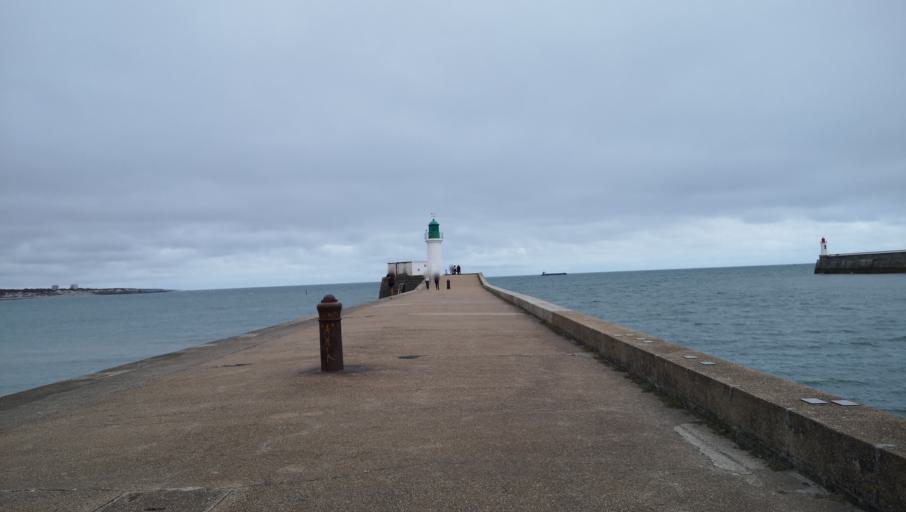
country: FR
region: Pays de la Loire
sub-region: Departement de la Vendee
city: Les Sables-d'Olonne
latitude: 46.4915
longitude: -1.7927
